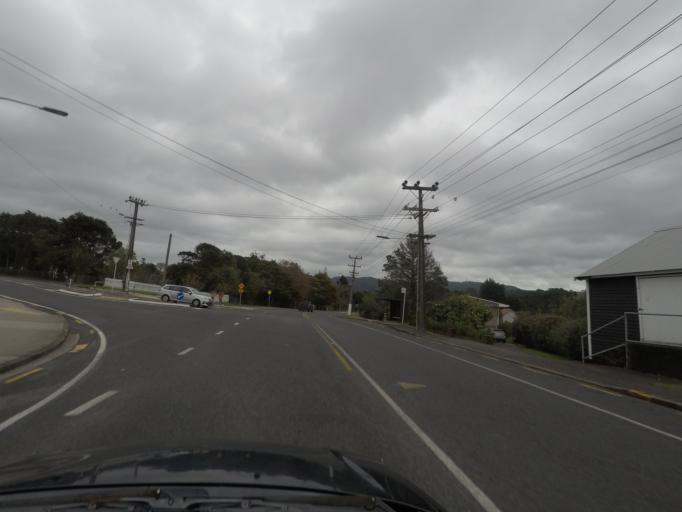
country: NZ
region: Auckland
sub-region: Auckland
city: Waitakere
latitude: -36.9114
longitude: 174.6216
